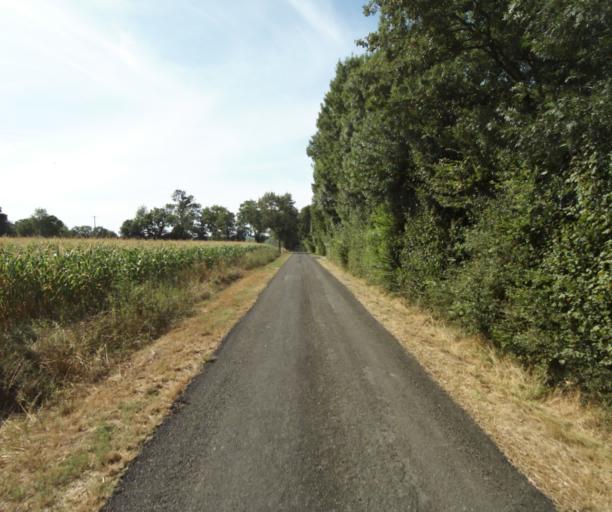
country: FR
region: Midi-Pyrenees
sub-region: Departement du Tarn
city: Soreze
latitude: 43.5098
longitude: 2.0555
